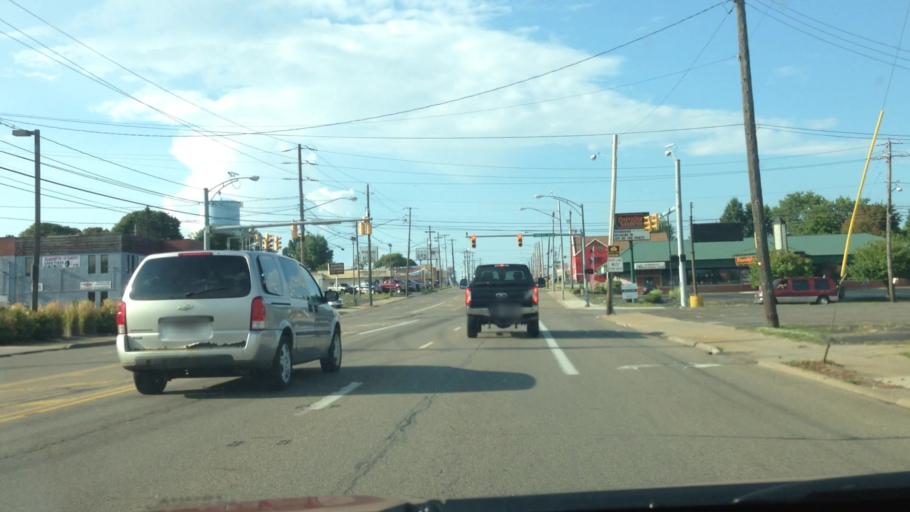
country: US
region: Ohio
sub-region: Summit County
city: Portage Lakes
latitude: 41.0409
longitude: -81.4912
